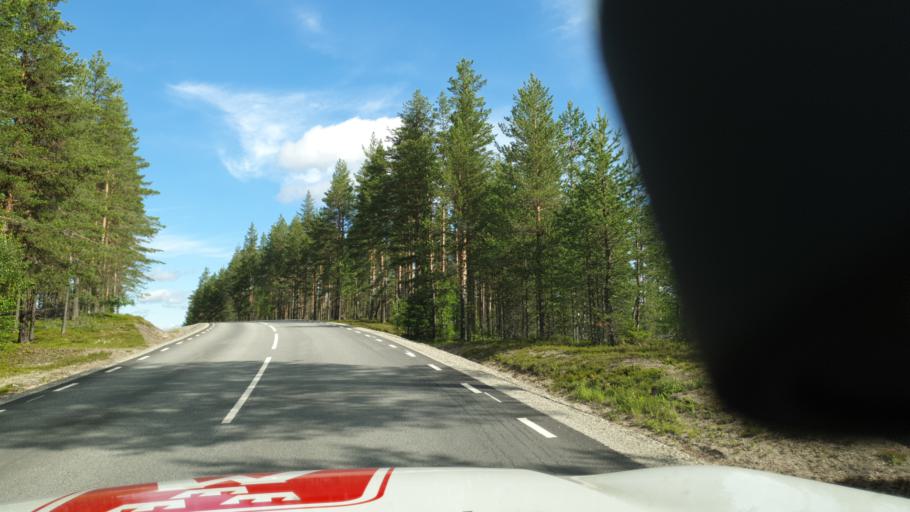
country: SE
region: Vaesterbotten
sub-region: Norsjo Kommun
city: Norsjoe
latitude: 64.6332
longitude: 19.2889
